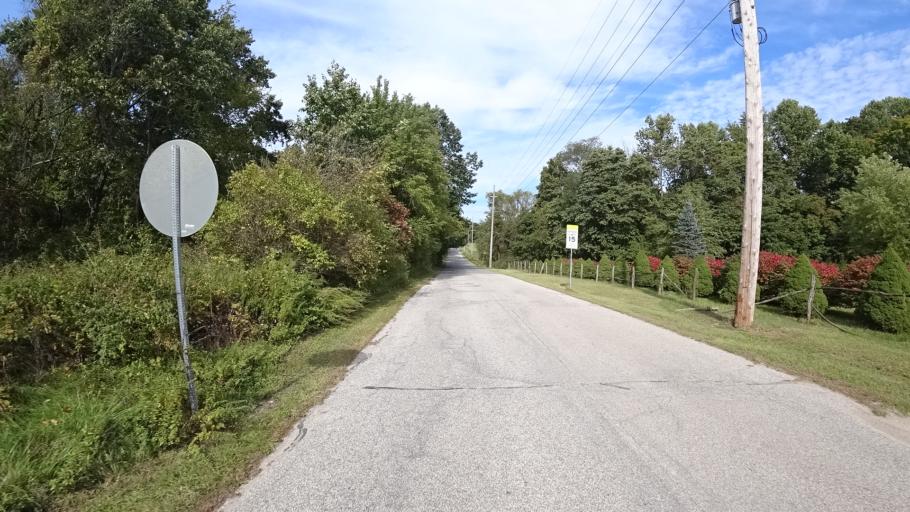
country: US
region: Indiana
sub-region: LaPorte County
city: Trail Creek
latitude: 41.7136
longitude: -86.8553
